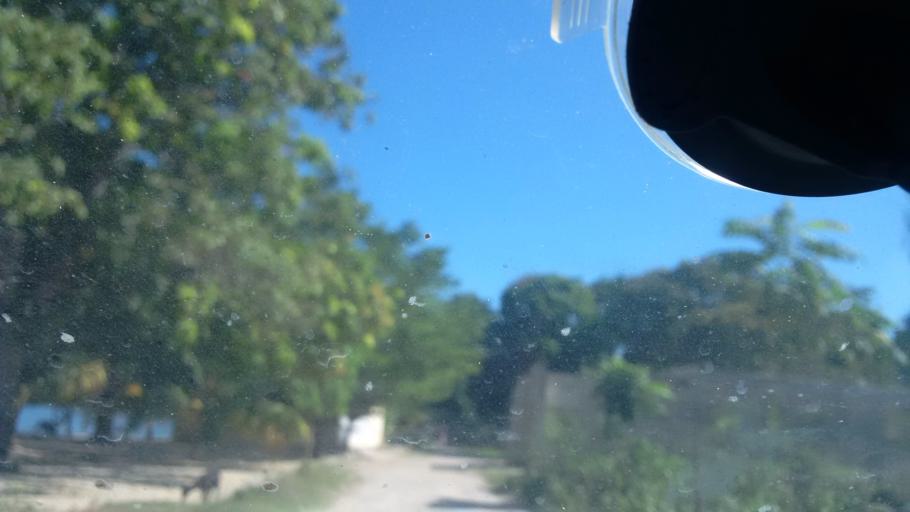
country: HT
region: Ouest
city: Grangwav
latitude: 18.4303
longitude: -72.7899
